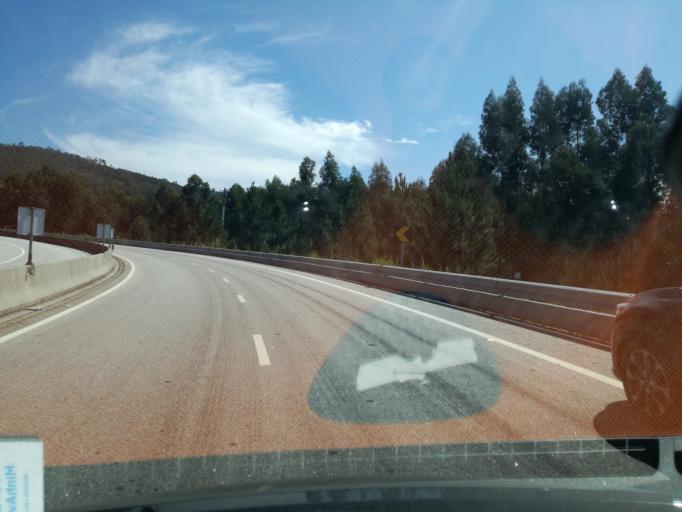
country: ES
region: Galicia
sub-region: Provincia de Pontevedra
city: O Rosal
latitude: 41.8773
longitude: -8.7941
